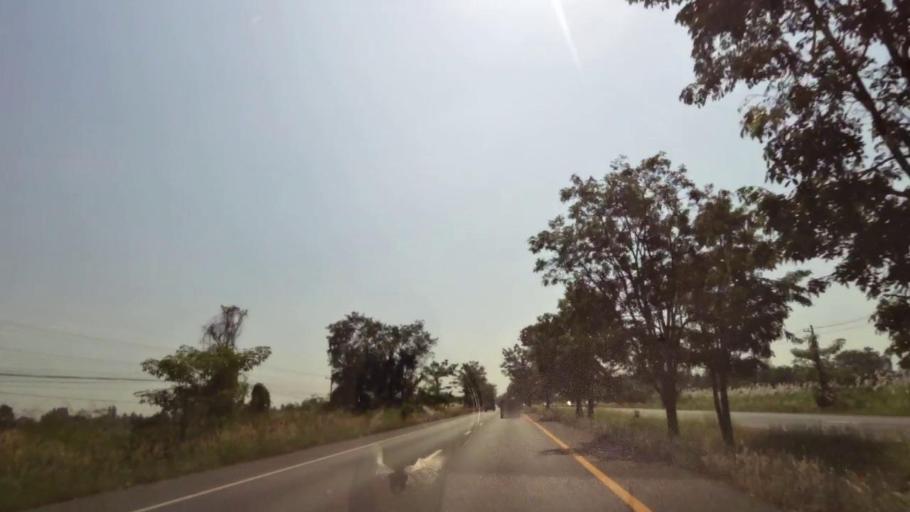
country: TH
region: Nakhon Sawan
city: Kao Liao
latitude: 15.9445
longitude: 100.1145
